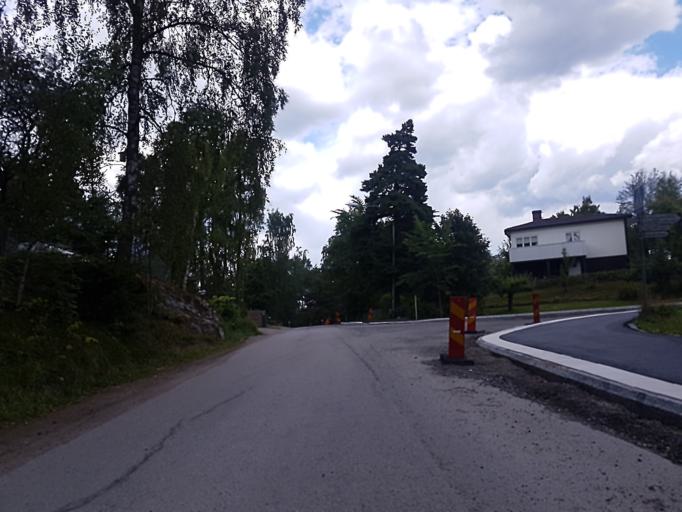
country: SE
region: Soedermanland
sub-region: Gnesta Kommun
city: Gnesta
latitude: 59.0442
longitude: 17.3118
